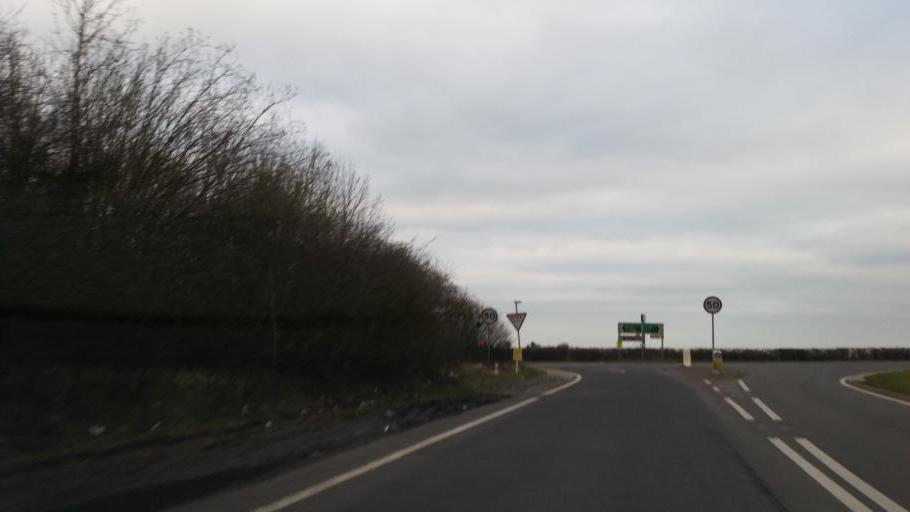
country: GB
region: England
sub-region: Northamptonshire
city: Brixworth
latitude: 52.4014
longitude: -0.9179
